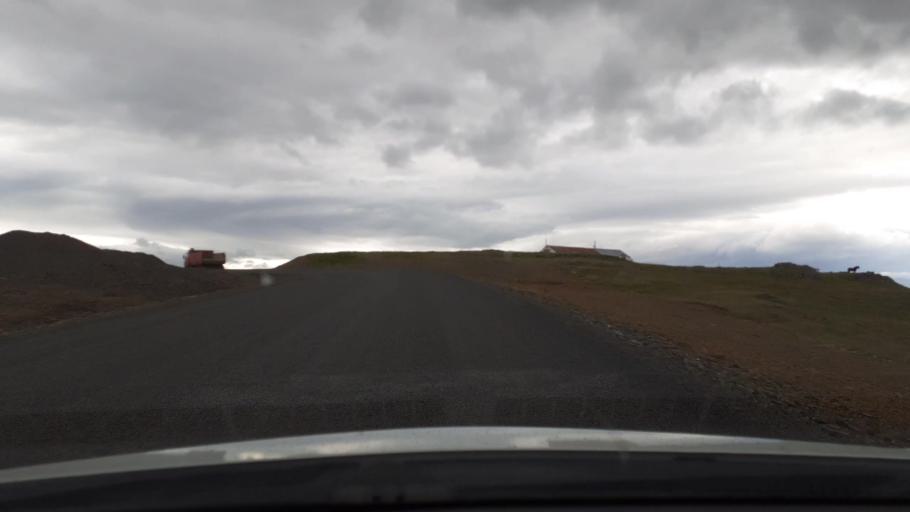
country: IS
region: West
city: Borgarnes
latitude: 64.6698
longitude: -21.7001
